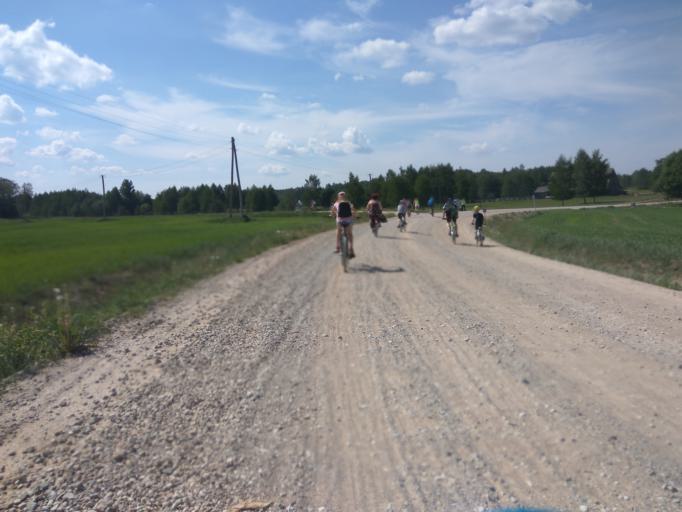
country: LV
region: Kuldigas Rajons
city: Kuldiga
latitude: 56.9400
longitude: 21.9727
